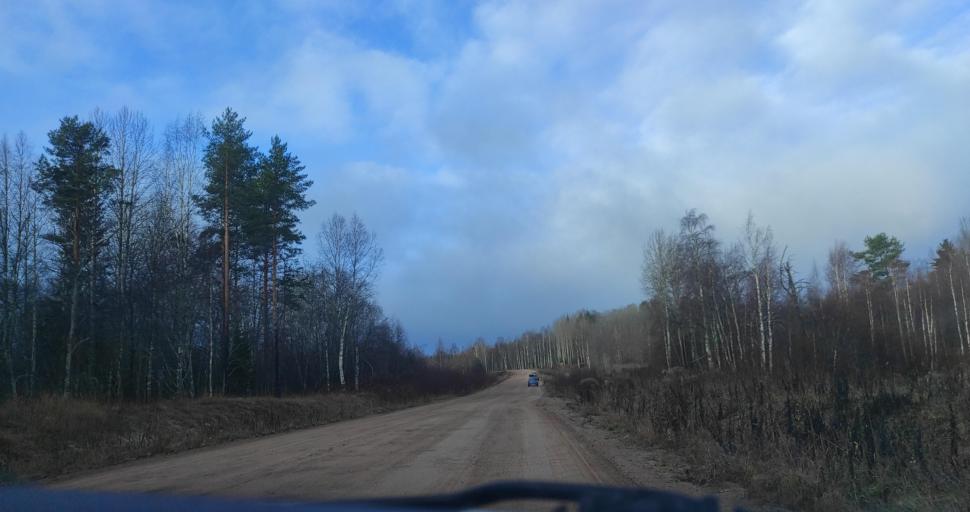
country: RU
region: Republic of Karelia
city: Pitkyaranta
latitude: 61.7120
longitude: 31.3579
